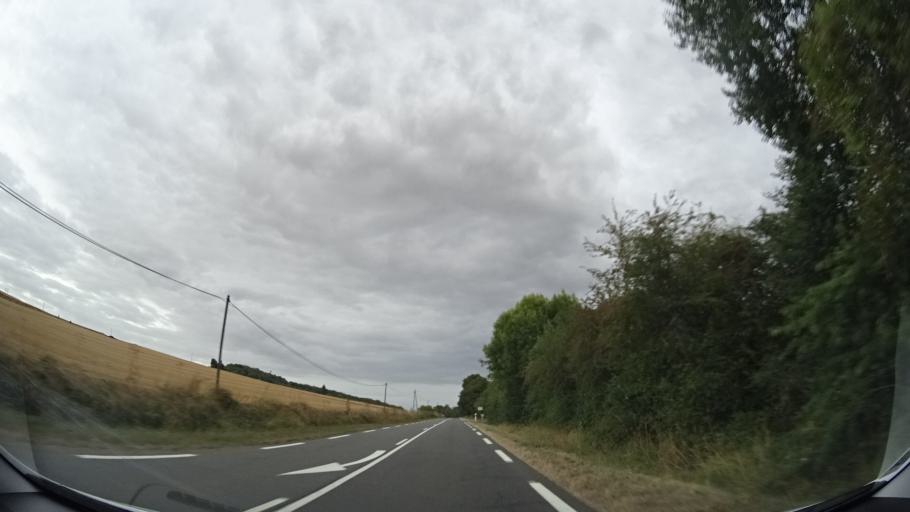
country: FR
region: Centre
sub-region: Departement du Loiret
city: Douchy
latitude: 47.9393
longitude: 3.0656
